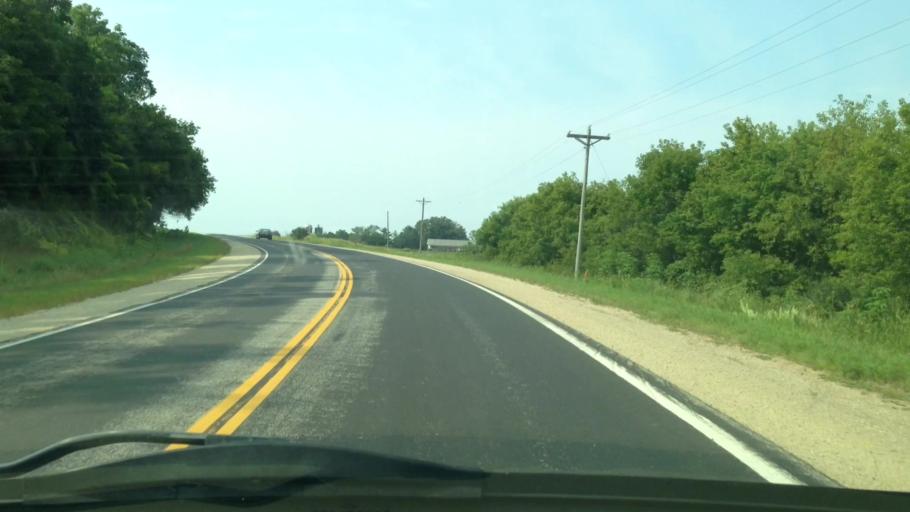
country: US
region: Minnesota
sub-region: Winona County
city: Lewiston
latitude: 43.9266
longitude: -91.9577
